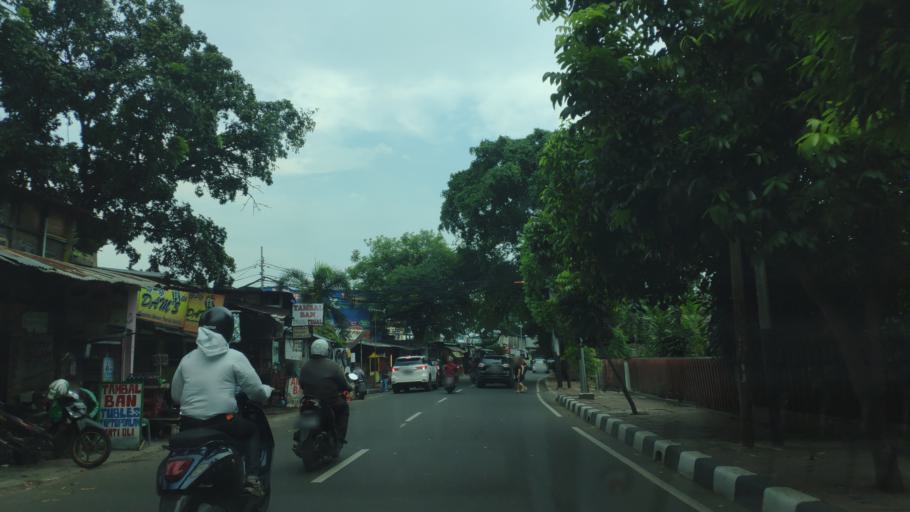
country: ID
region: Jakarta Raya
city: Jakarta
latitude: -6.1908
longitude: 106.7824
